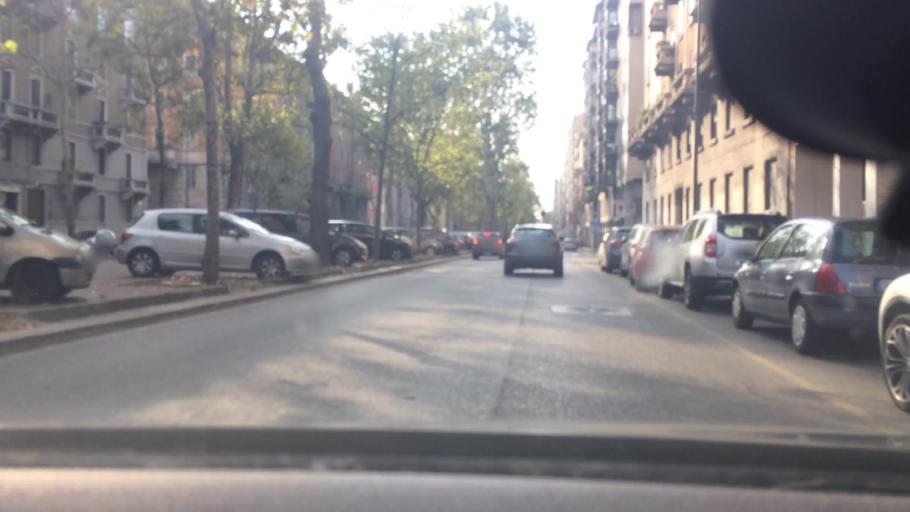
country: IT
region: Lombardy
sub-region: Citta metropolitana di Milano
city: Milano
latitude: 45.4887
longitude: 9.2106
